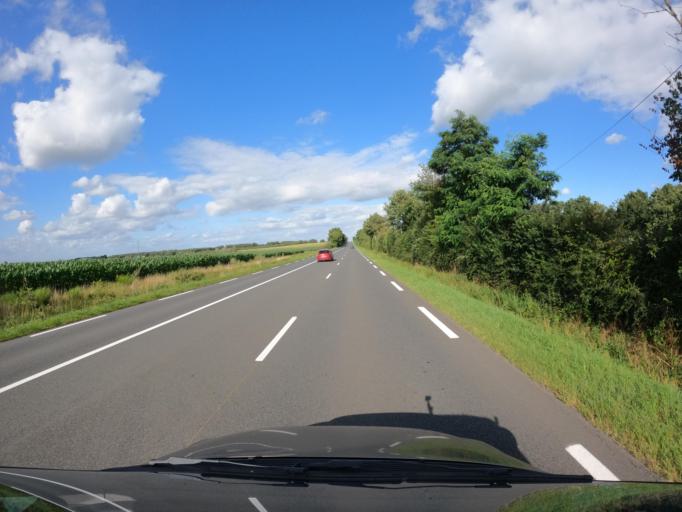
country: FR
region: Pays de la Loire
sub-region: Departement de Maine-et-Loire
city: Nueil-sur-Layon
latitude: 47.1623
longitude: -0.3923
